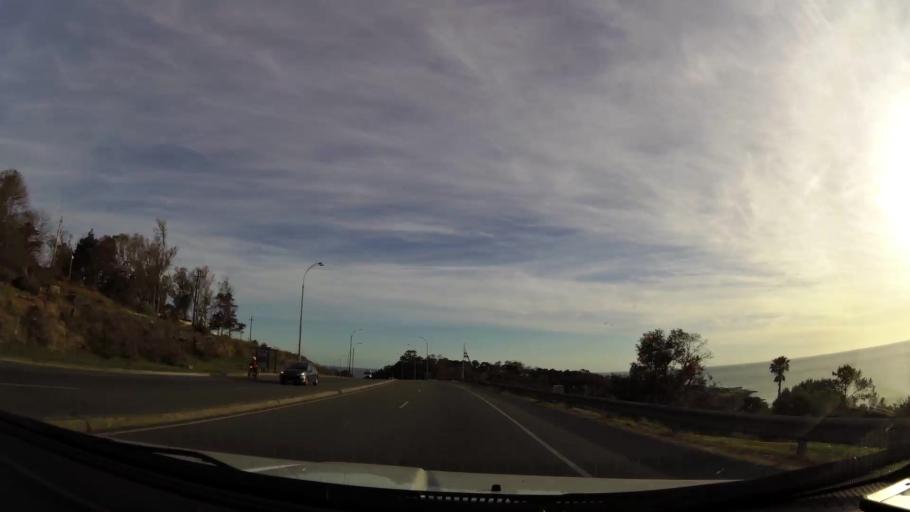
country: UY
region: Maldonado
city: Maldonado
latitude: -34.8946
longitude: -55.0383
